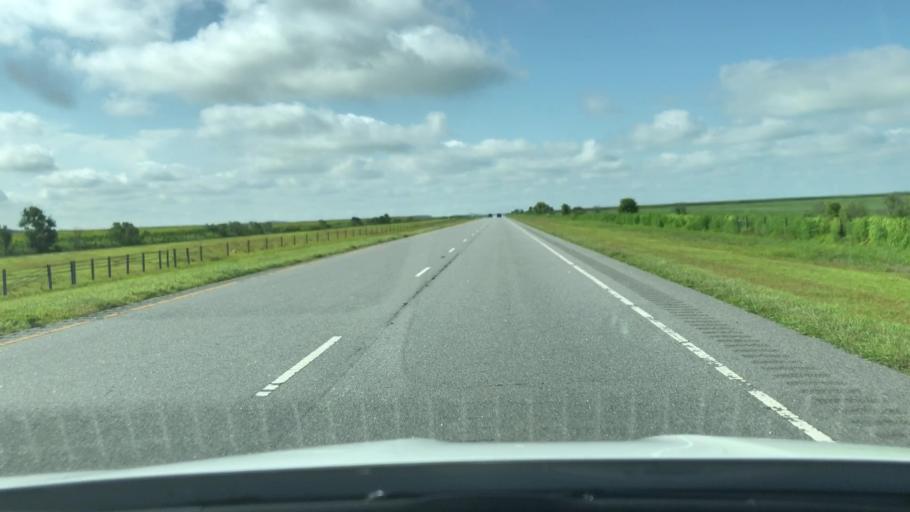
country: US
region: North Carolina
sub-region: Pasquotank County
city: Elizabeth City
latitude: 36.3533
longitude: -76.3147
